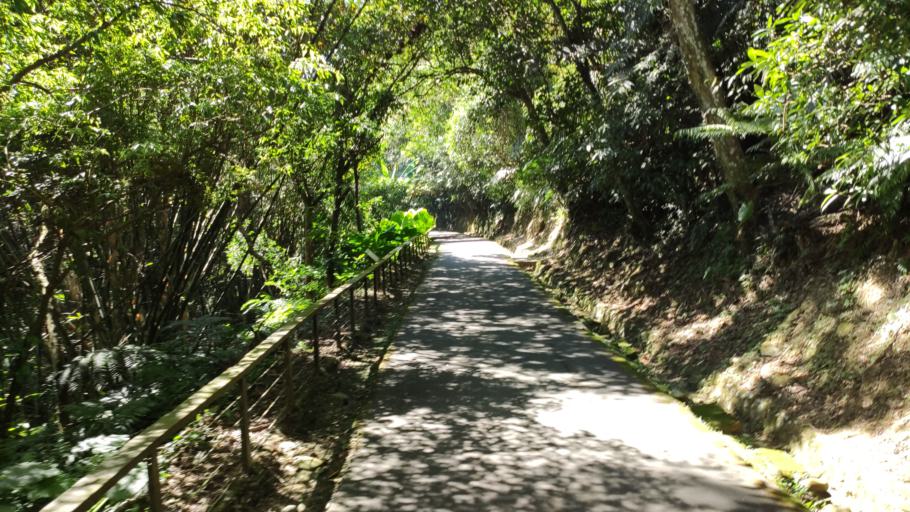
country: TW
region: Taiwan
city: Daxi
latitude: 24.8419
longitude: 121.3068
